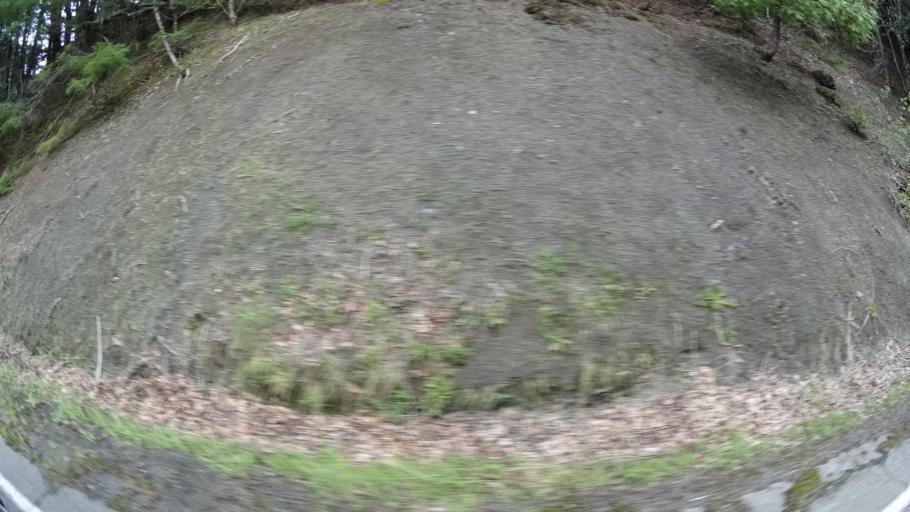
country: US
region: California
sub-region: Humboldt County
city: Willow Creek
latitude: 40.8901
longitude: -123.7697
